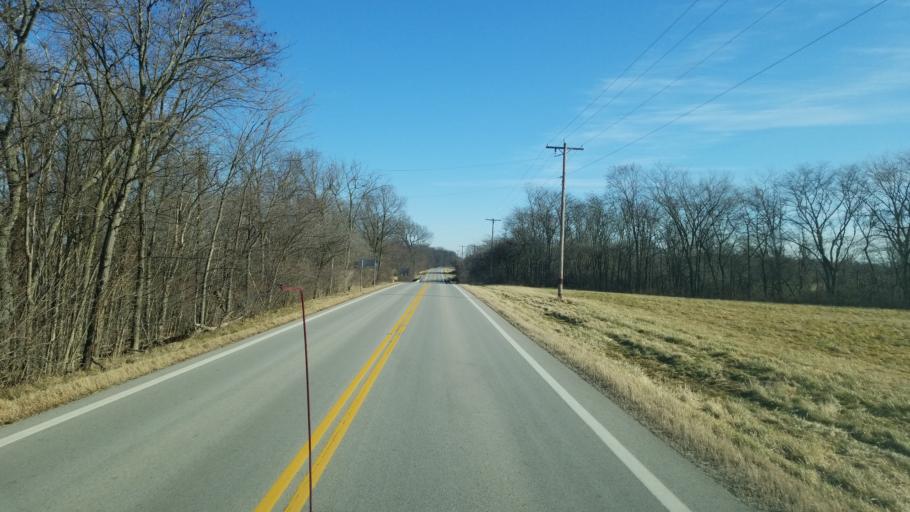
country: US
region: Ohio
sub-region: Henry County
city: Liberty Center
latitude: 41.4151
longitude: -83.9405
